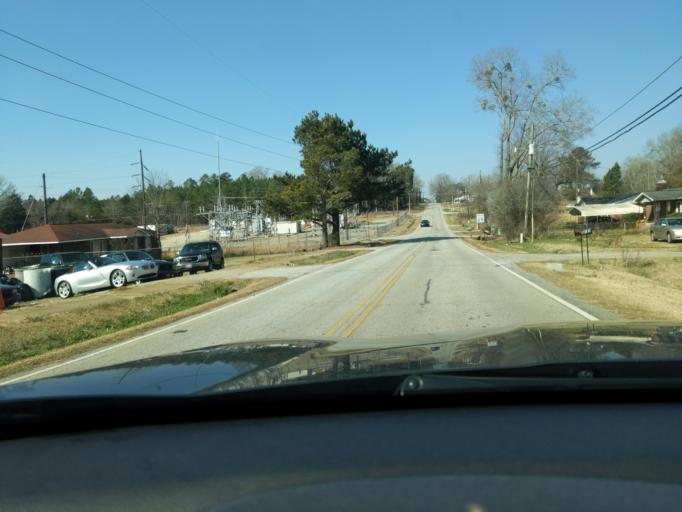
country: US
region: South Carolina
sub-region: Abbeville County
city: Calhoun Falls
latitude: 34.0875
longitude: -82.5872
